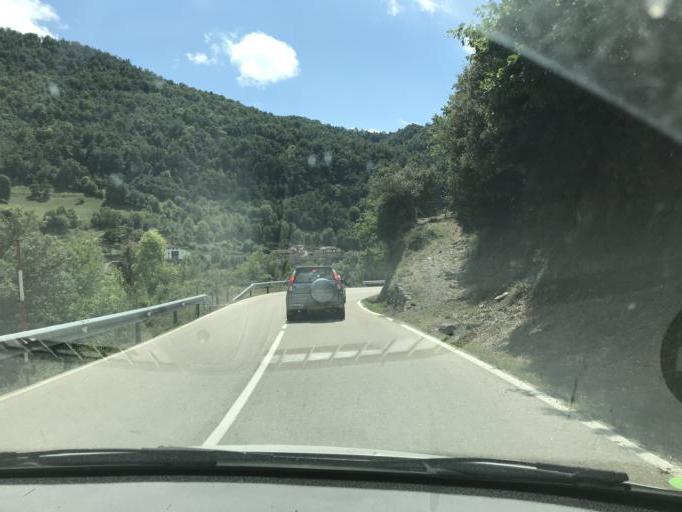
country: ES
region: Cantabria
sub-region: Provincia de Cantabria
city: Cabezon de Liebana
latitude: 43.0763
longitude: -4.5234
